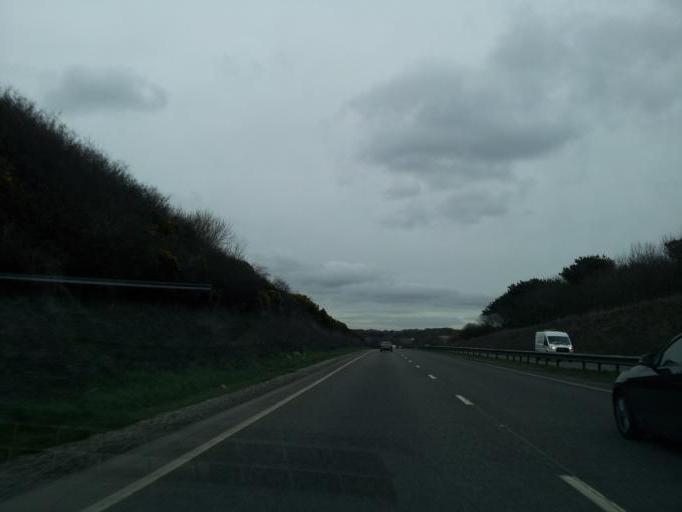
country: GB
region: England
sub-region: Cornwall
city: Redruth
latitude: 50.2515
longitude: -5.2091
